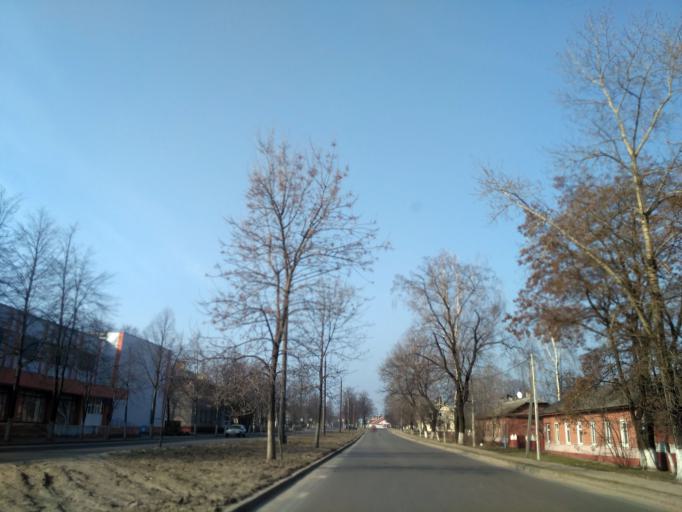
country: BY
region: Minsk
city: Horad Barysaw
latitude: 54.2281
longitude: 28.5105
